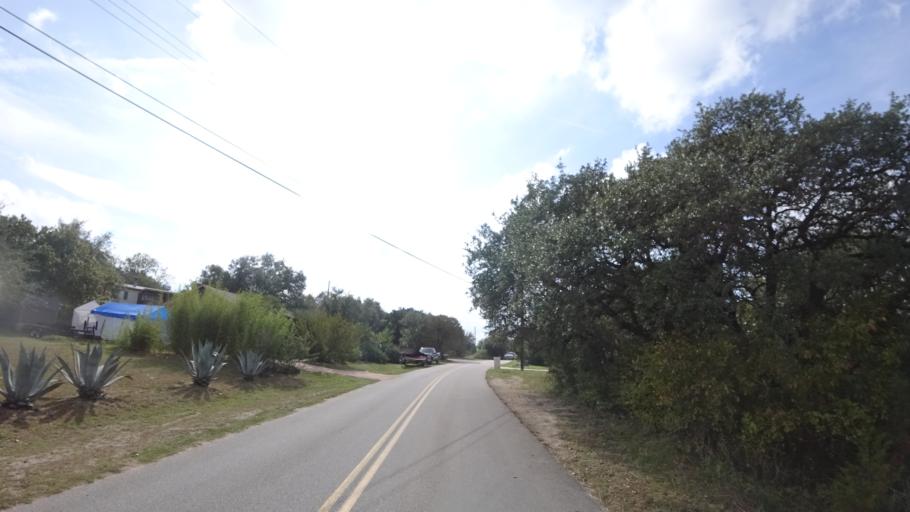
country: US
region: Texas
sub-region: Travis County
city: Hudson Bend
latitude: 30.3800
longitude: -97.9317
